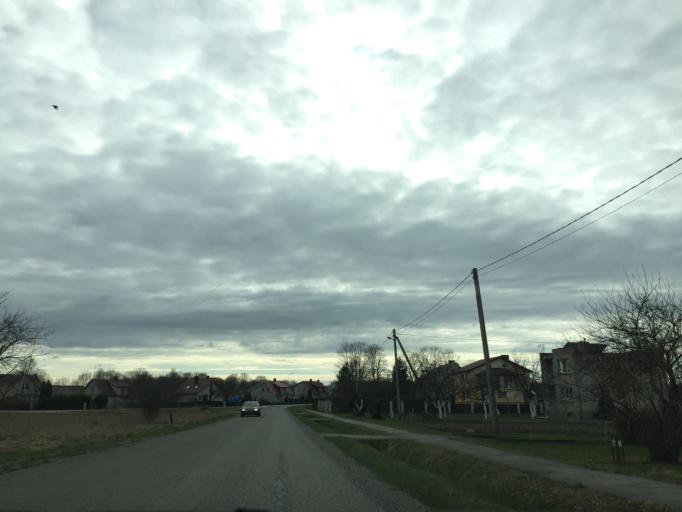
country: LT
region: Klaipedos apskritis
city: Gargzdai
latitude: 55.7197
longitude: 21.4851
